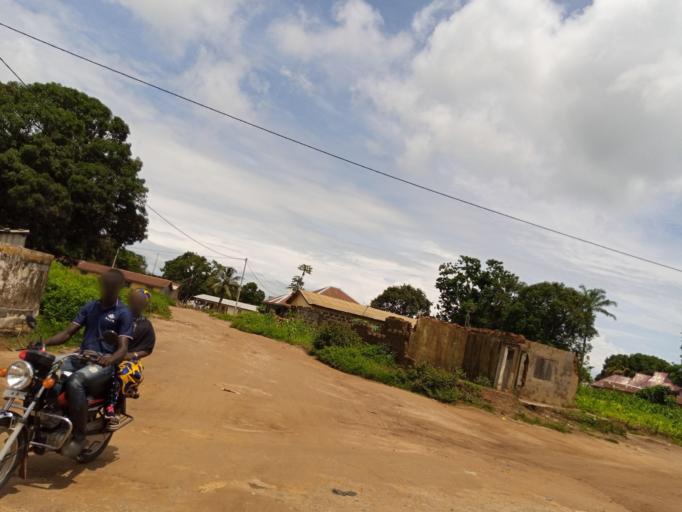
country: SL
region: Northern Province
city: Masoyila
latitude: 8.6093
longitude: -13.1894
